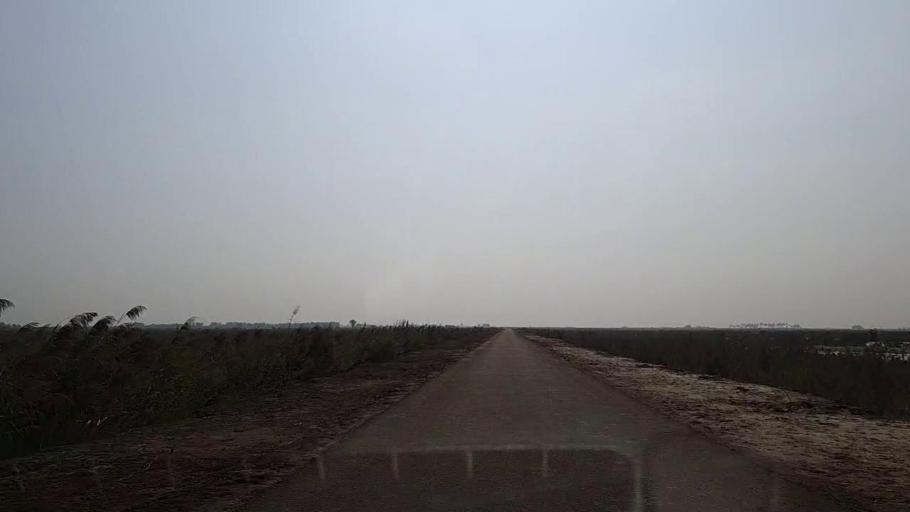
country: PK
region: Sindh
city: Gharo
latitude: 24.6674
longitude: 67.6951
